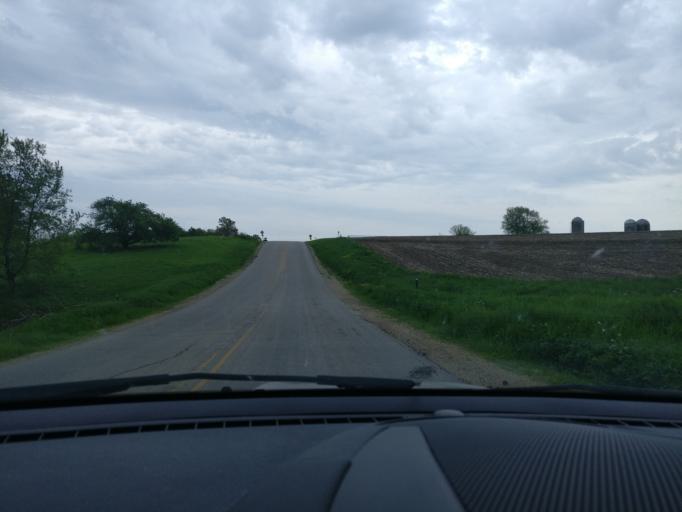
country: US
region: Wisconsin
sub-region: Lafayette County
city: Darlington
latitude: 42.7514
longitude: -89.9941
